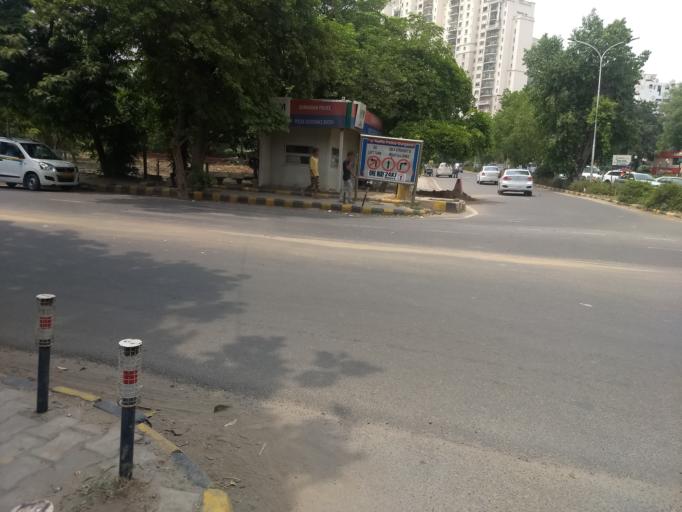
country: IN
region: Haryana
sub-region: Gurgaon
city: Gurgaon
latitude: 28.4617
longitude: 77.0870
